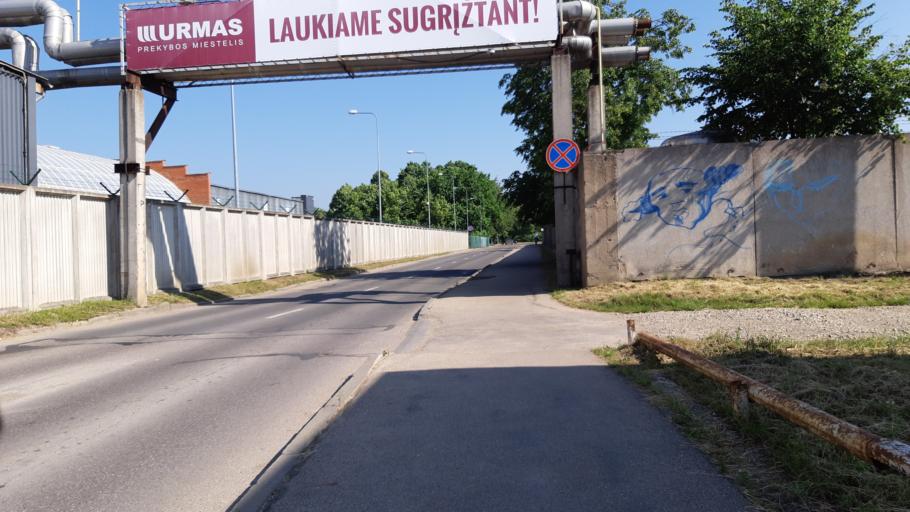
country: LT
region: Kauno apskritis
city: Dainava (Kaunas)
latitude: 54.9168
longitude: 23.9918
